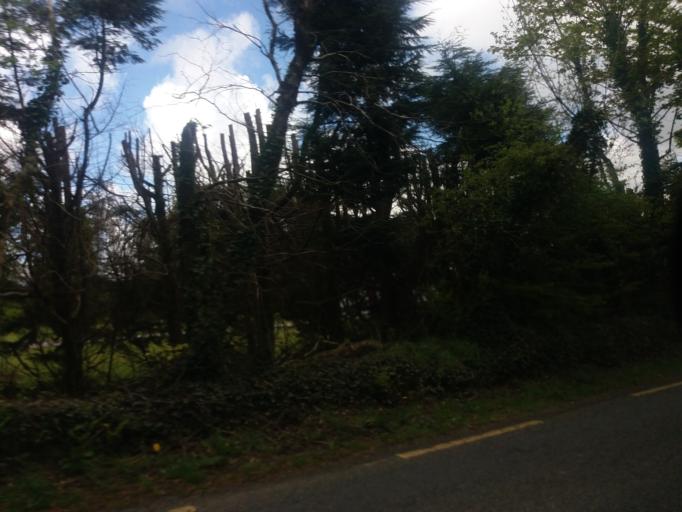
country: IE
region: Leinster
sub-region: Loch Garman
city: Loch Garman
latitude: 52.3036
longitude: -6.5583
